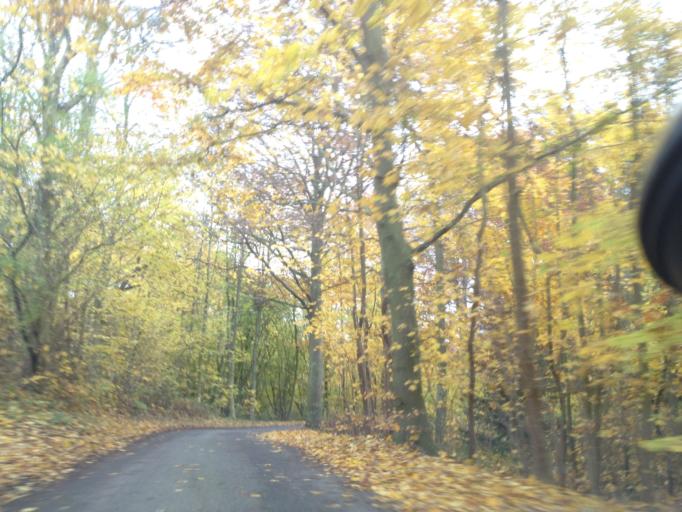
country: DK
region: South Denmark
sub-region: Assens Kommune
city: Vissenbjerg
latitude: 55.4343
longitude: 10.1681
